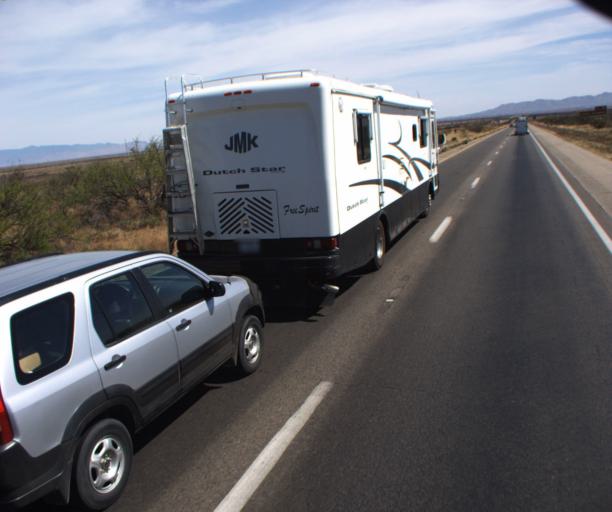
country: US
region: Arizona
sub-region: Cochise County
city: Willcox
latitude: 32.1684
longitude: -109.9625
